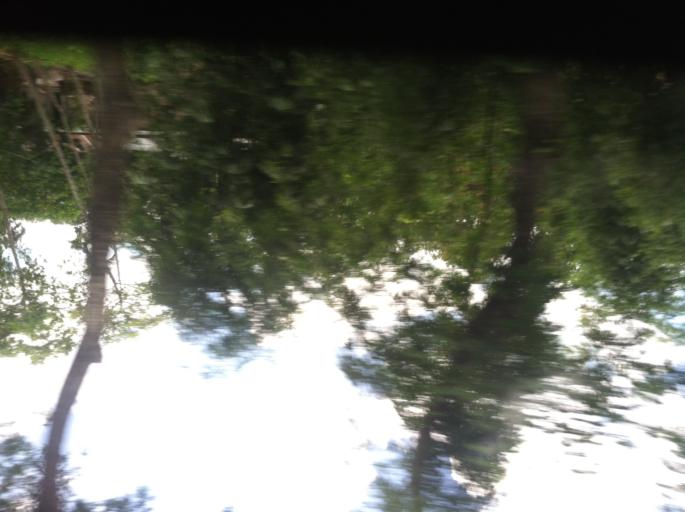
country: BD
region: Sylhet
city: Habiganj
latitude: 24.2212
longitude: 91.3643
